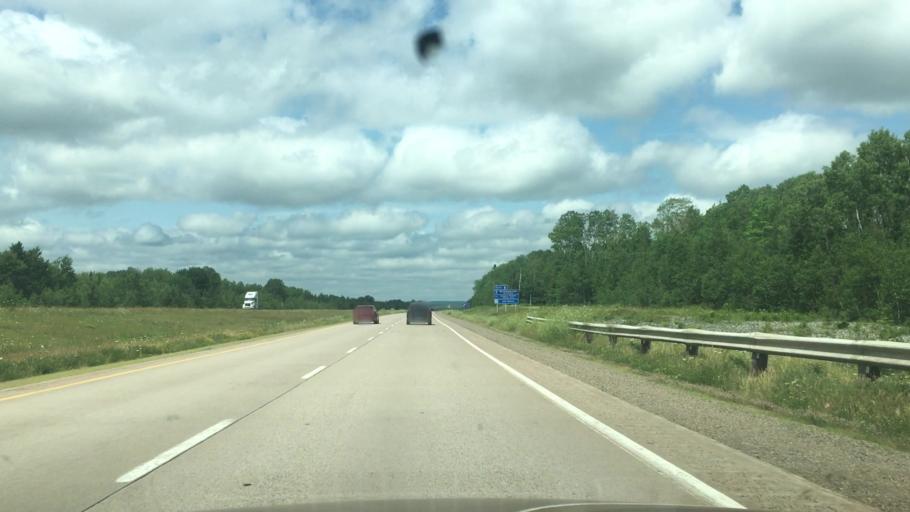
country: CA
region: Nova Scotia
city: Oxford
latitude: 45.7084
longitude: -63.8263
